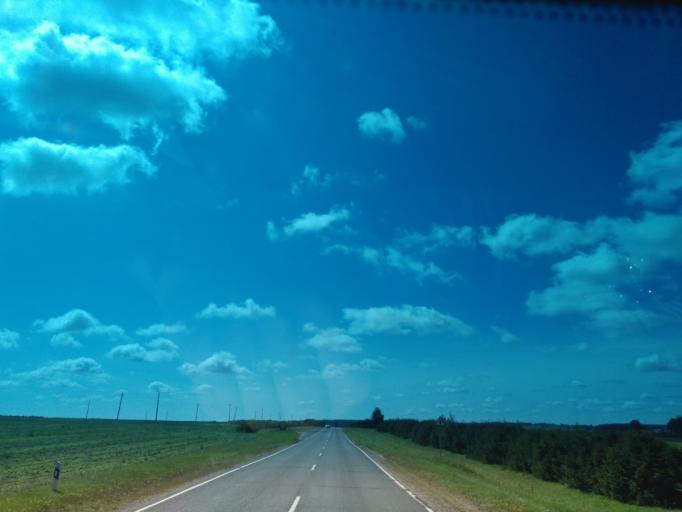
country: BY
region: Minsk
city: Uzda
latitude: 53.3779
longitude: 27.2377
